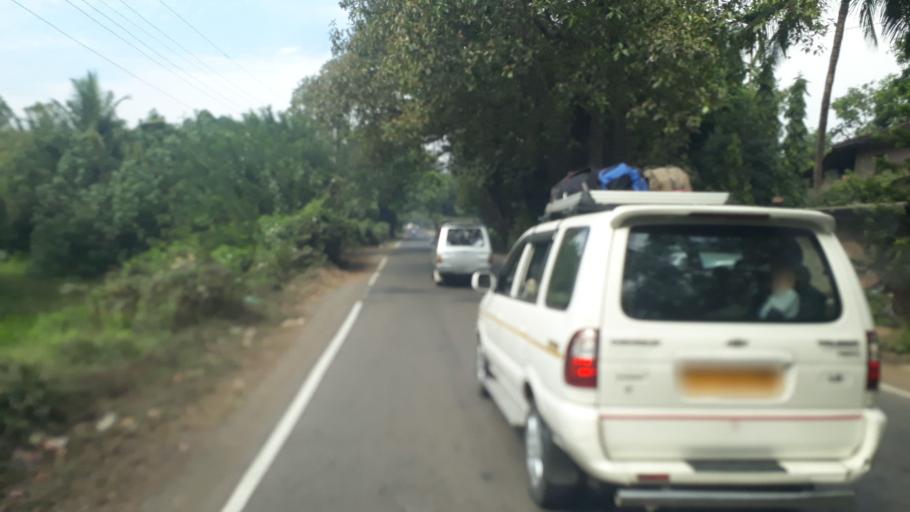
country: IN
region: Maharashtra
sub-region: Raigarh
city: Alibag
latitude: 18.6932
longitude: 72.9652
